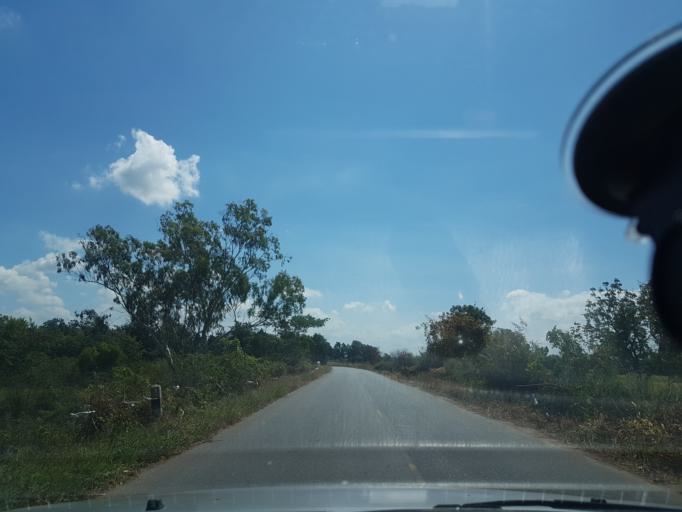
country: TH
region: Lop Buri
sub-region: Amphoe Tha Luang
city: Tha Luang
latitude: 15.0006
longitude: 101.0054
